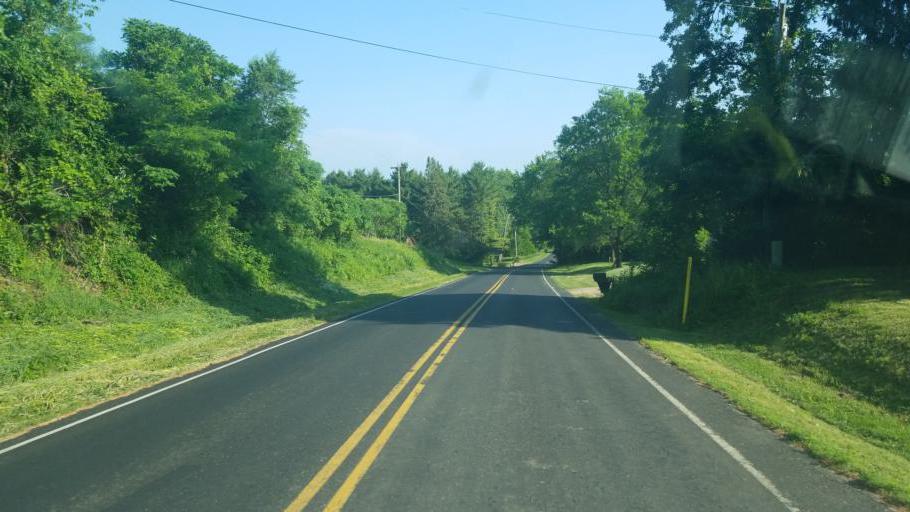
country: US
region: Wisconsin
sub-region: Vernon County
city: Hillsboro
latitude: 43.6618
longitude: -90.3462
